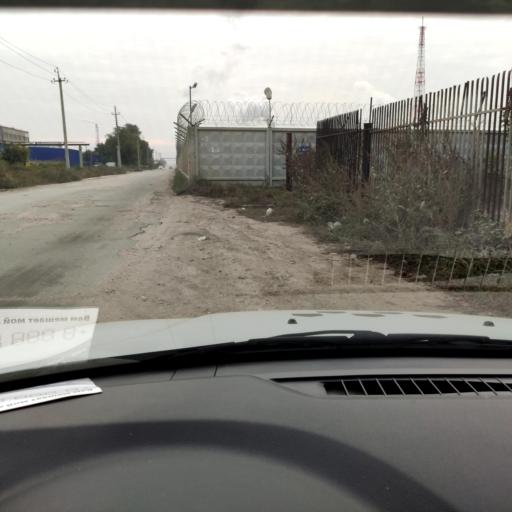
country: RU
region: Samara
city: Tol'yatti
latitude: 53.5592
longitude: 49.4555
